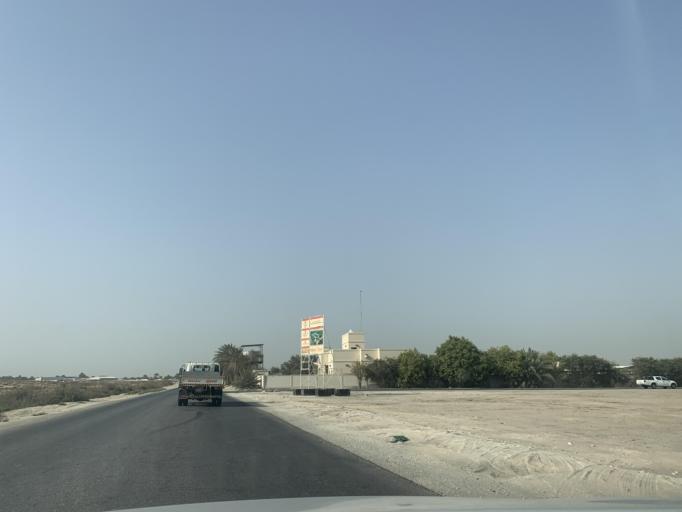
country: BH
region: Central Governorate
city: Madinat Hamad
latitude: 26.1567
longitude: 50.4880
